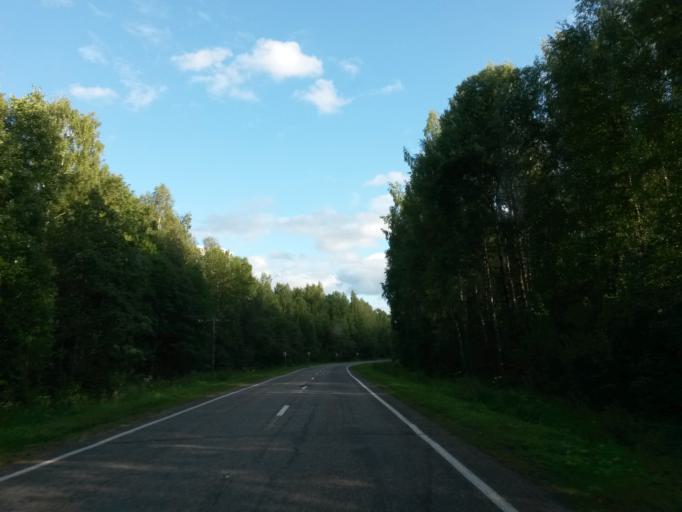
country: RU
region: Jaroslavl
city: Tutayev
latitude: 57.9183
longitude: 39.5148
